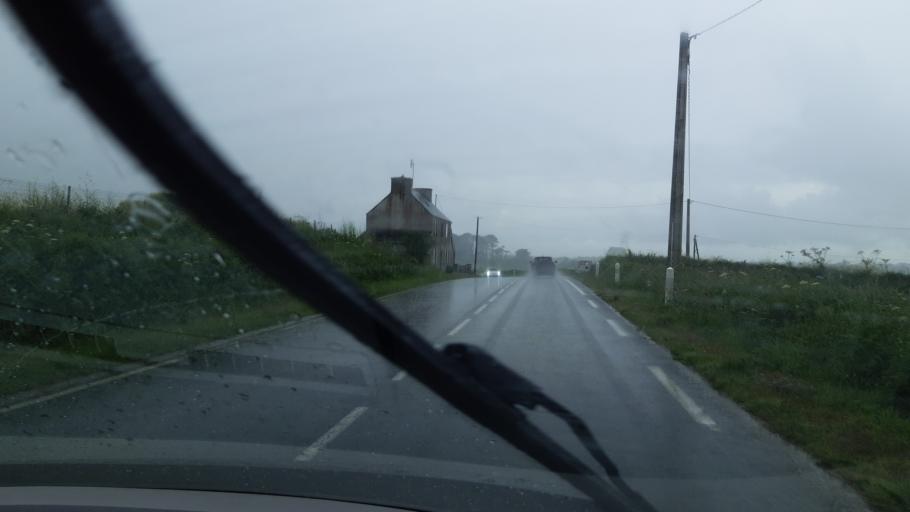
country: FR
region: Brittany
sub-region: Departement du Finistere
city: Plougoulm
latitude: 48.6659
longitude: -4.0172
